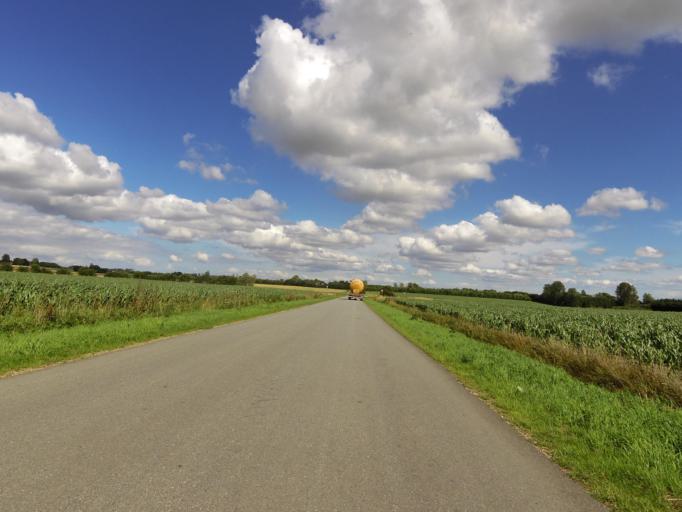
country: DK
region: South Denmark
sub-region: Vejen Kommune
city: Rodding
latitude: 55.3154
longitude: 9.1682
